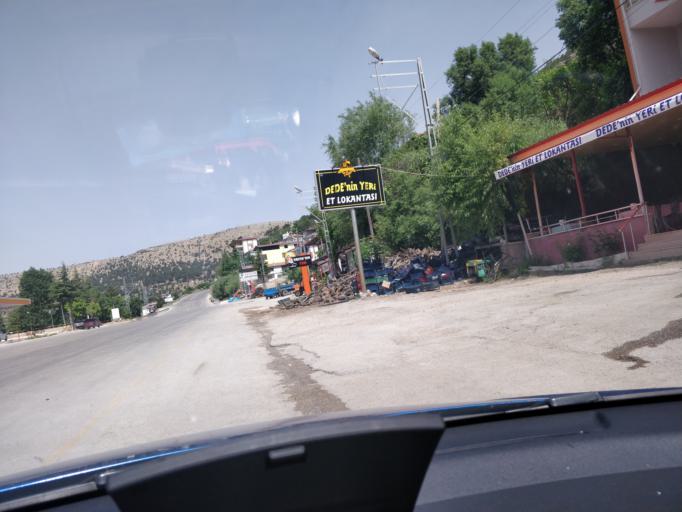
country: TR
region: Karaman
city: Bucakkisla
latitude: 36.8847
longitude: 33.2797
